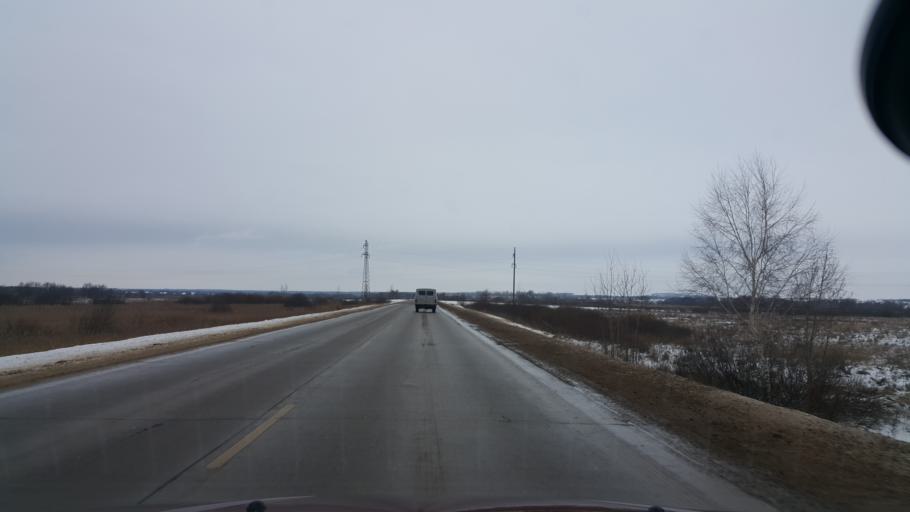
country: RU
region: Tambov
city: Bokino
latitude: 52.6233
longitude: 41.4848
